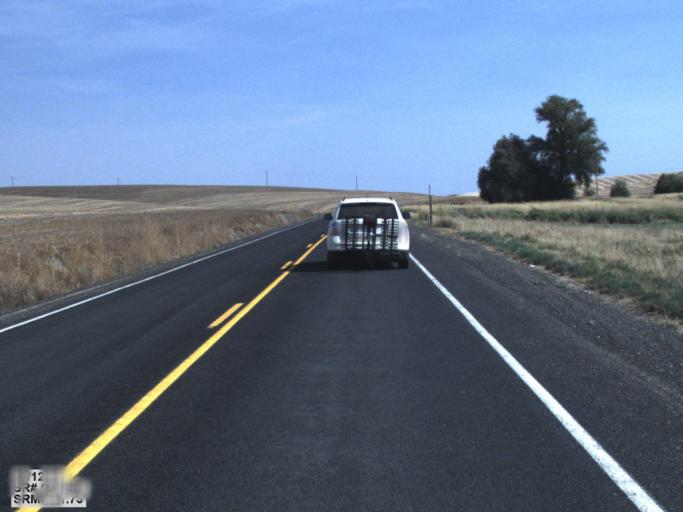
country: US
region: Idaho
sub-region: Benewah County
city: Plummer
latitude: 47.1804
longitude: -117.1779
